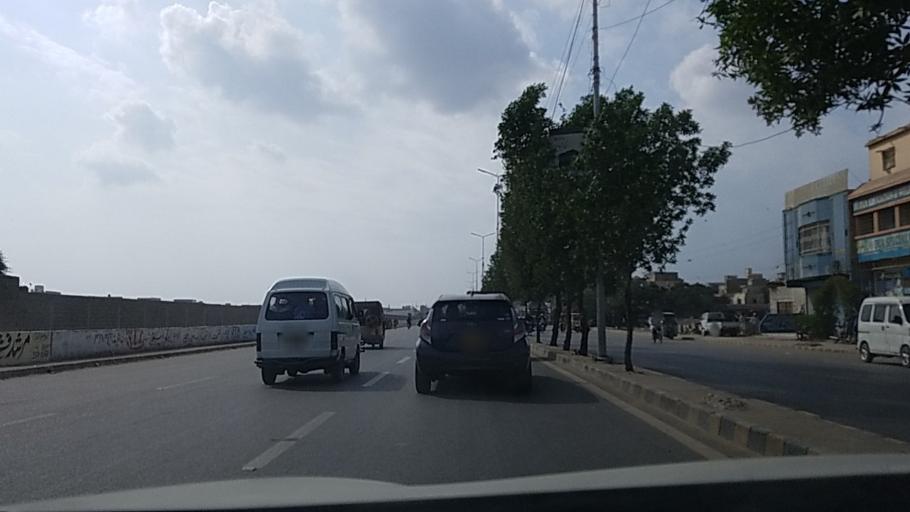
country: PK
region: Sindh
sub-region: Karachi District
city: Karachi
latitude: 24.8214
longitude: 67.1295
